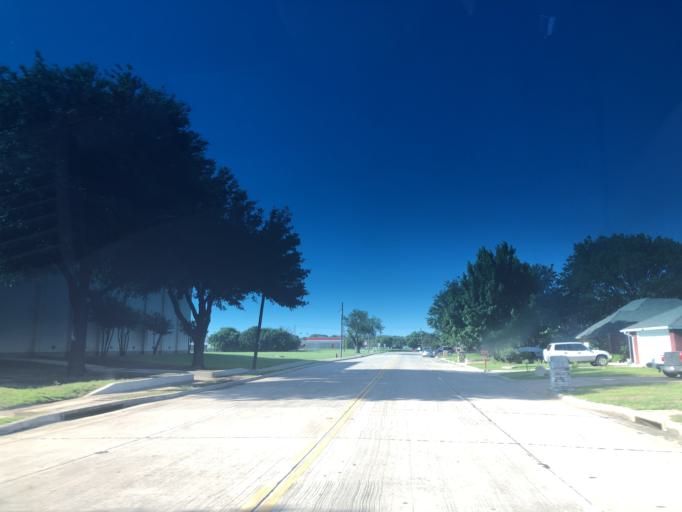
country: US
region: Texas
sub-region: Dallas County
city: Grand Prairie
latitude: 32.7128
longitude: -97.0018
